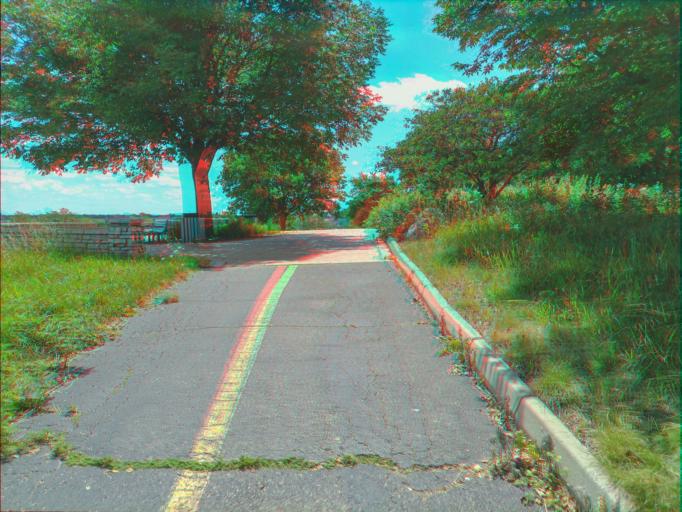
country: US
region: Illinois
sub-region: Lake County
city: Long Grove
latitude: 42.1448
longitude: -87.9957
